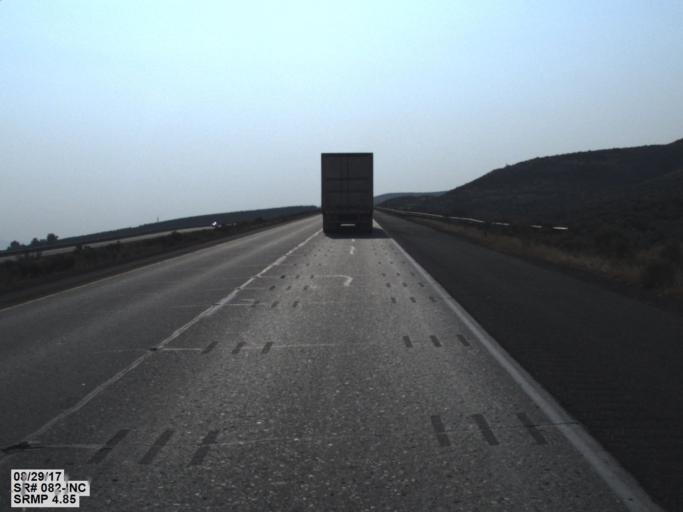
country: US
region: Washington
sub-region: Kittitas County
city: Kittitas
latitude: 46.9117
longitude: -120.4728
